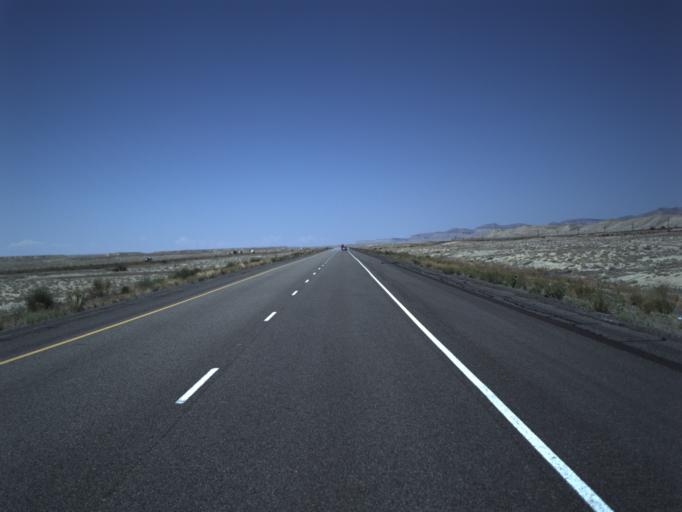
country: US
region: Utah
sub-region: Grand County
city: Moab
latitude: 38.9337
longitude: -109.4409
